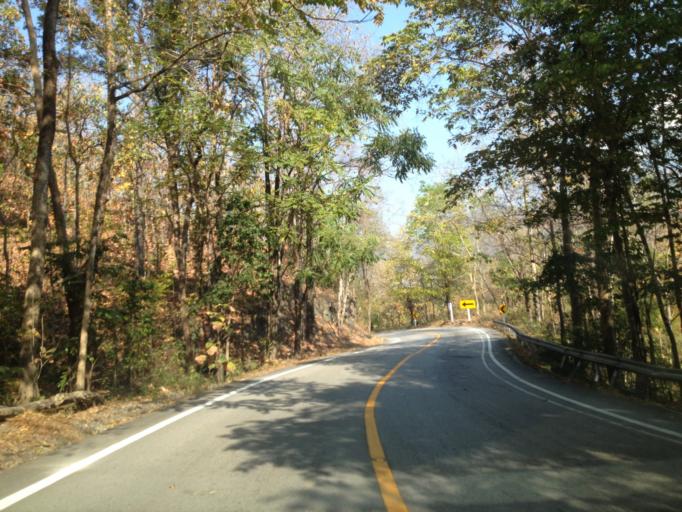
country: TH
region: Chiang Mai
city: Hot
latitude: 18.2008
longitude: 98.4509
